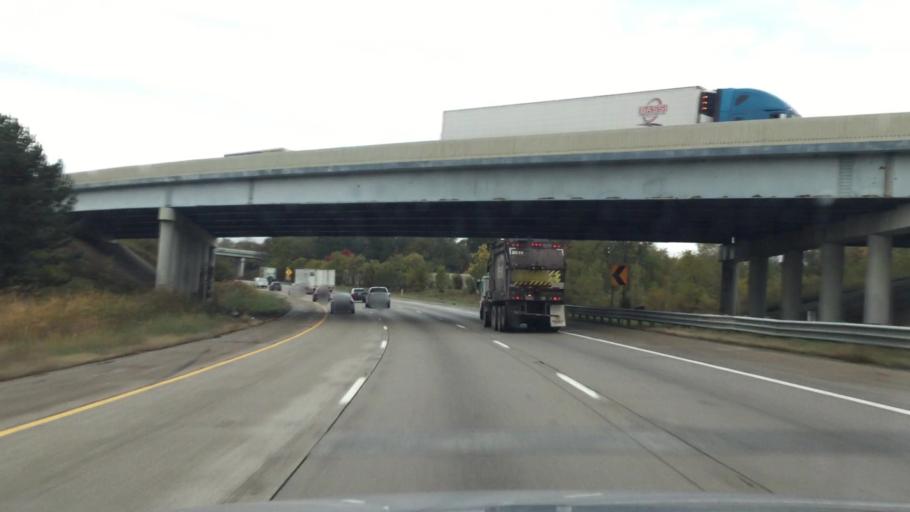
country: US
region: Michigan
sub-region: Washtenaw County
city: Ypsilanti
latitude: 42.2314
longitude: -83.5784
